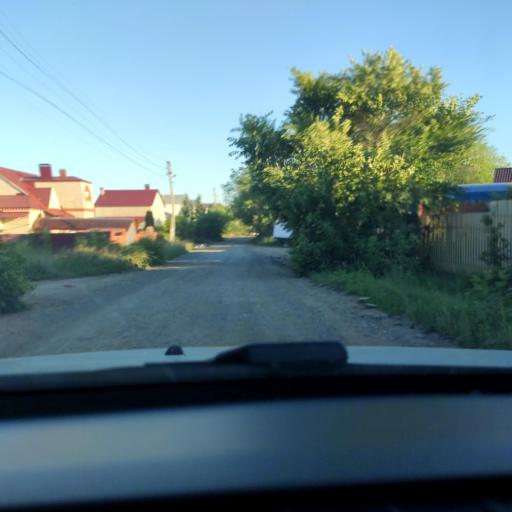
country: RU
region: Samara
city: Kinel'
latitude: 53.2722
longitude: 50.5924
